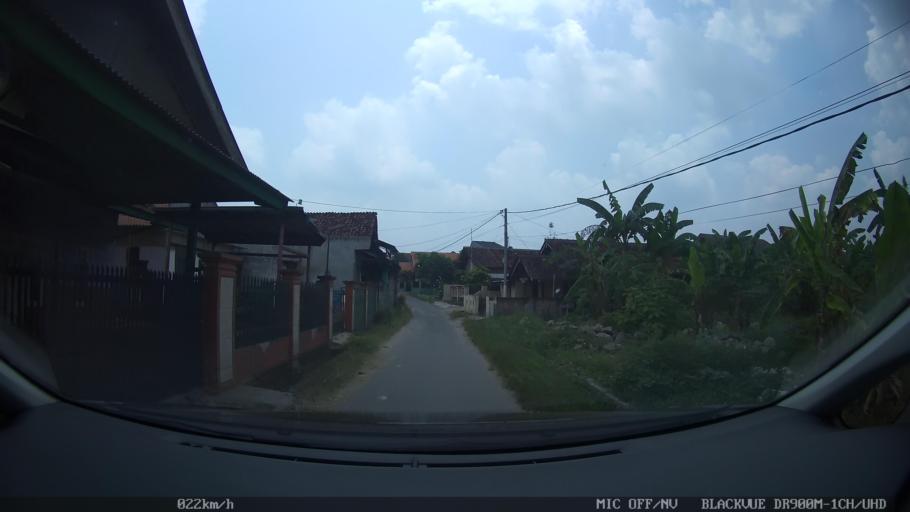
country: ID
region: Lampung
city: Pringsewu
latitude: -5.3466
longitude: 104.9768
